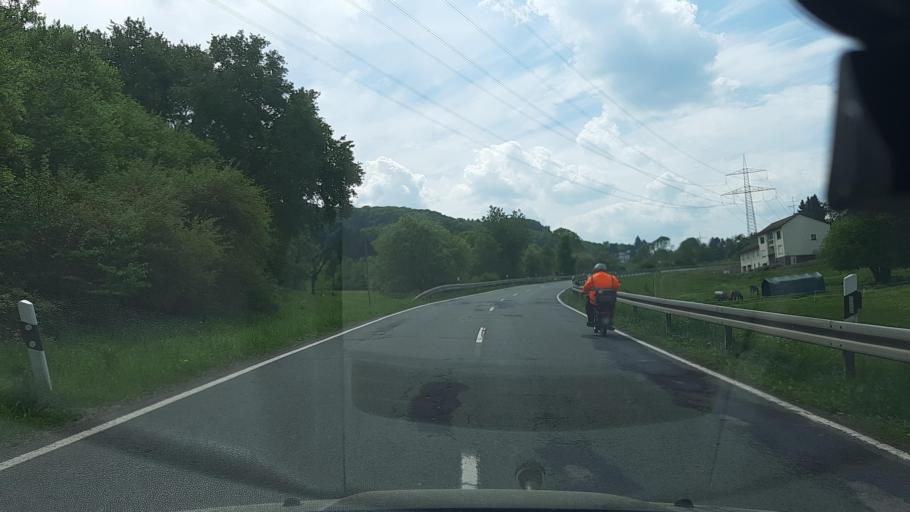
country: DE
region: Hesse
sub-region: Regierungsbezirk Giessen
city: Greifenstein
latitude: 50.6076
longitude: 8.3236
